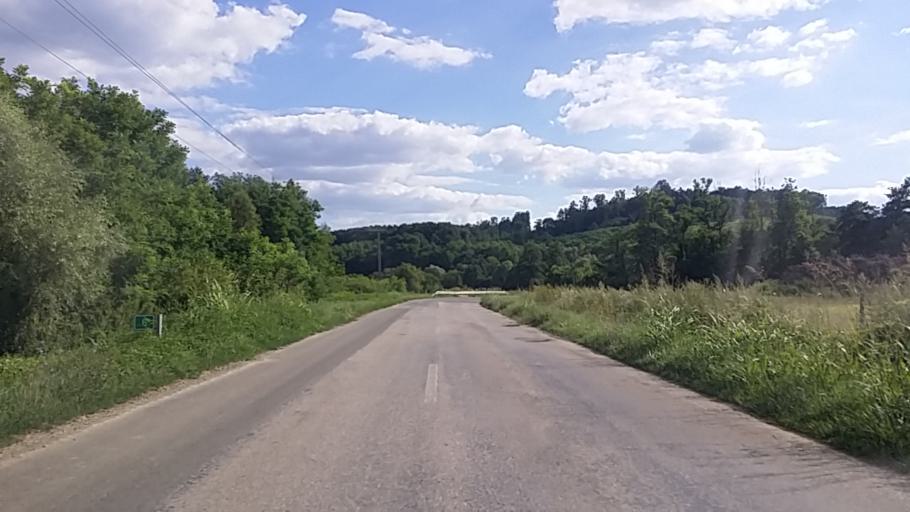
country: HU
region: Baranya
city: Sasd
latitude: 46.1882
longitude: 18.0823
